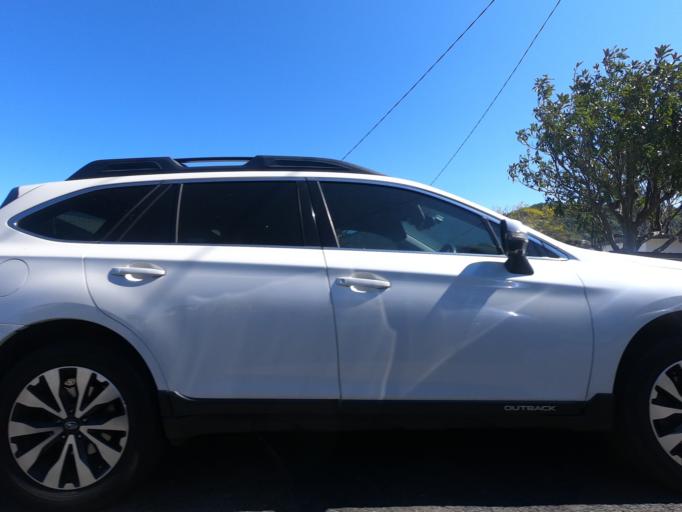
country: AU
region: New South Wales
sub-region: Wollongong
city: Mount Keira
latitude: -34.4267
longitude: 150.8507
